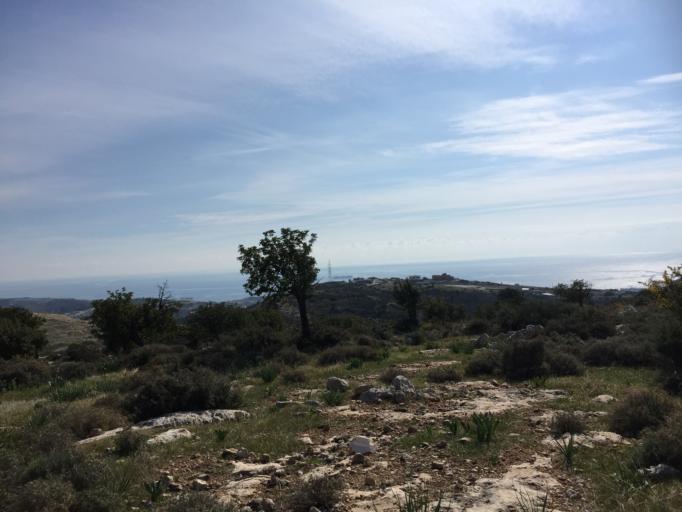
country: CY
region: Larnaka
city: Agios Tychon
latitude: 34.7402
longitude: 33.1232
